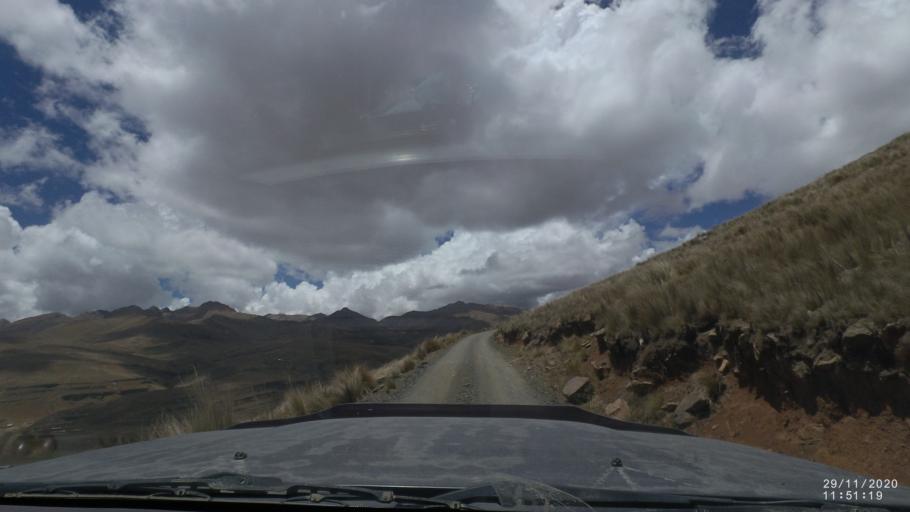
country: BO
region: Cochabamba
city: Cochabamba
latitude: -17.1718
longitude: -66.2604
